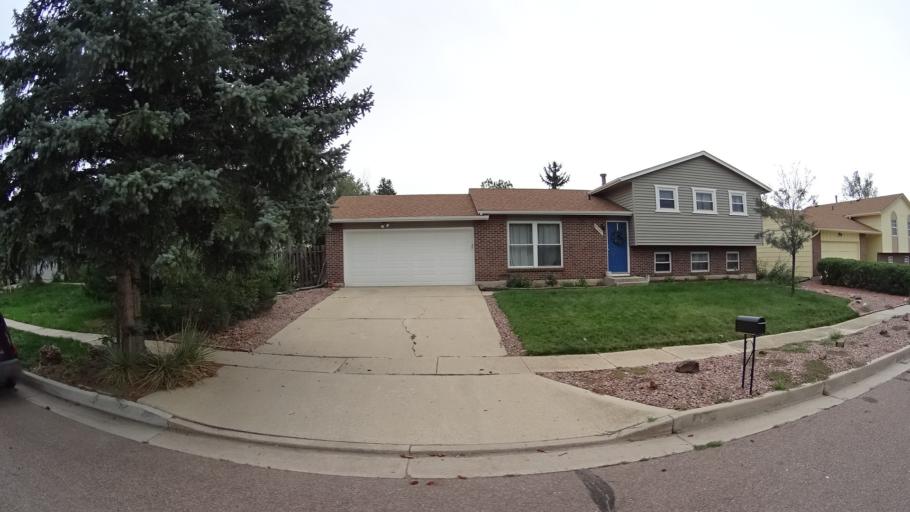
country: US
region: Colorado
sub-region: El Paso County
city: Air Force Academy
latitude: 38.9262
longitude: -104.7999
